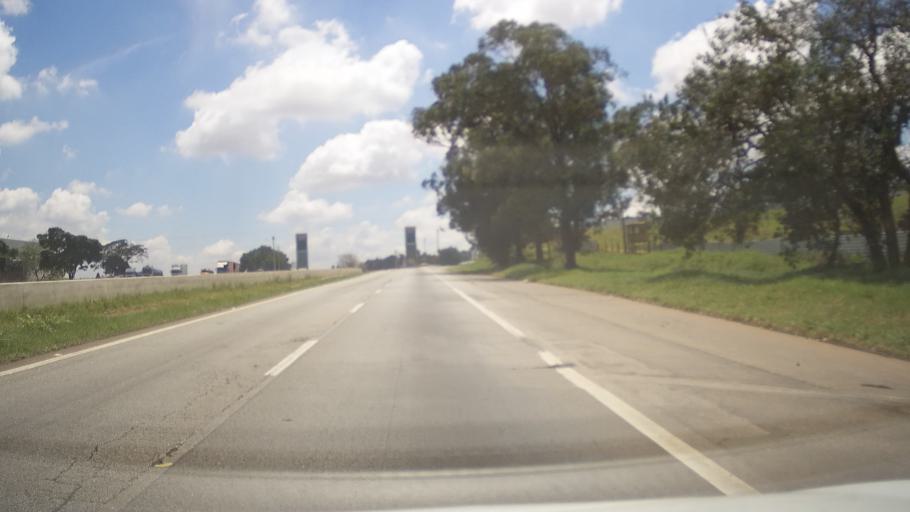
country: BR
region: Minas Gerais
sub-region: Sao Goncalo Do Sapucai
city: Sao Goncalo do Sapucai
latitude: -21.9475
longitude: -45.6218
